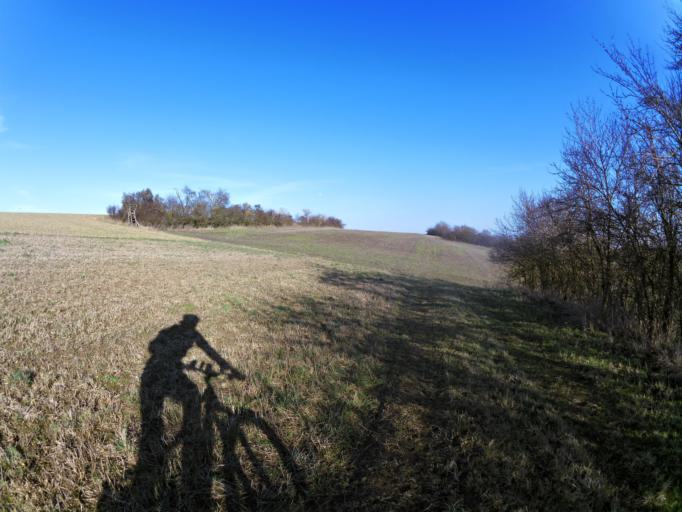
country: DE
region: Bavaria
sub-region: Regierungsbezirk Unterfranken
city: Giebelstadt
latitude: 49.6733
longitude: 9.9744
